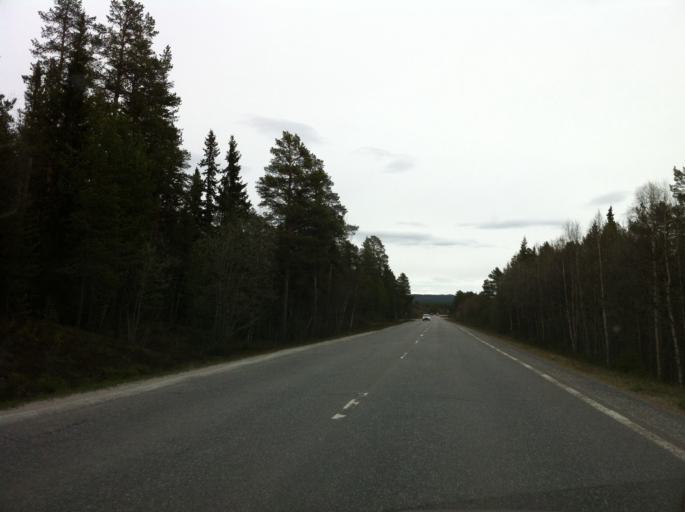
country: NO
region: Hedmark
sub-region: Engerdal
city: Engerdal
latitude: 62.5313
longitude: 12.5668
